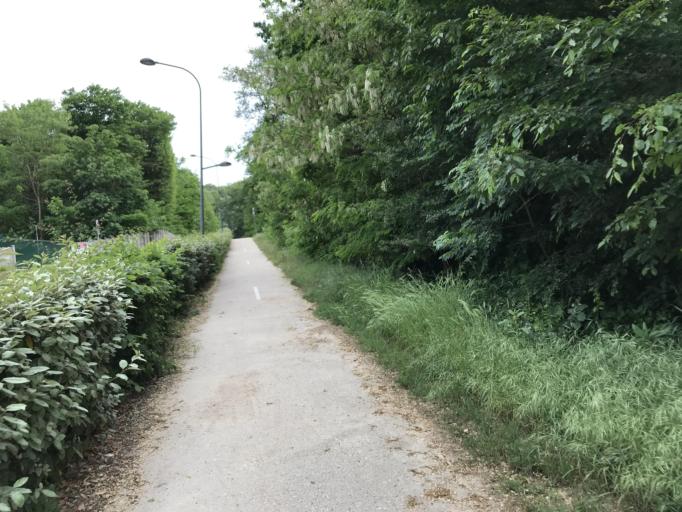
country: FR
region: Ile-de-France
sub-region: Departement de l'Essonne
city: La Ville-du-Bois
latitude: 48.6620
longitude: 2.2578
